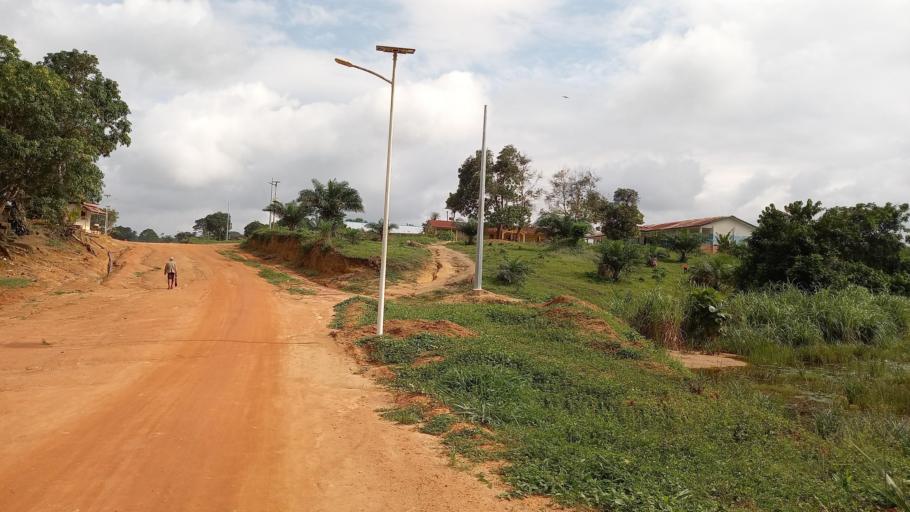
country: SL
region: Eastern Province
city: Kailahun
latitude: 8.2892
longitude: -10.5740
